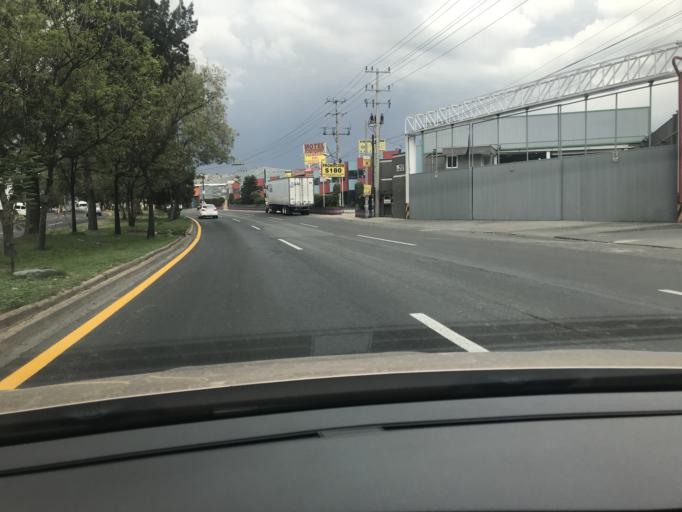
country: MX
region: Mexico
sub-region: La Paz
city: El Pino
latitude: 19.3552
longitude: -98.9583
